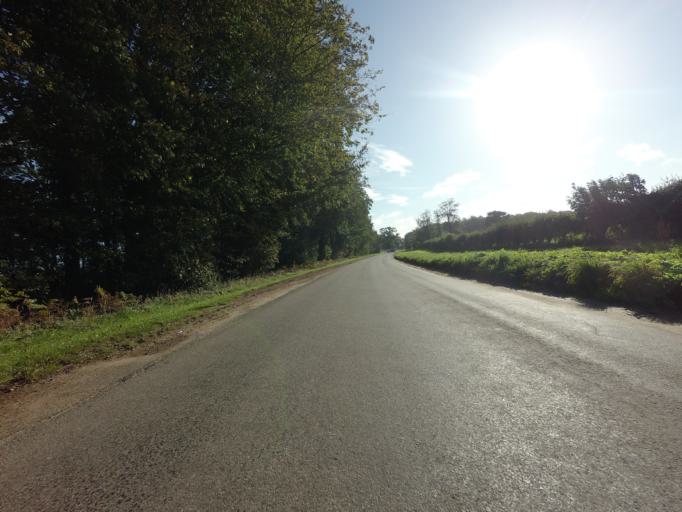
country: GB
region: England
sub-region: Norfolk
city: Dersingham
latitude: 52.8194
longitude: 0.6486
